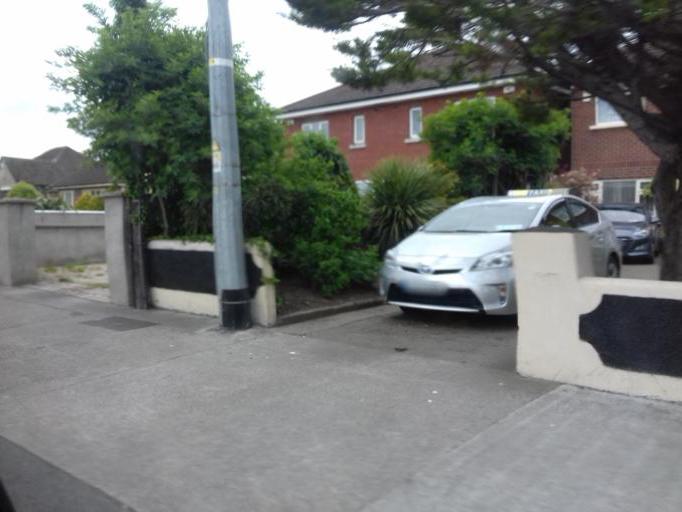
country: IE
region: Leinster
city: Crumlin
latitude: 53.3194
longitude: -6.3321
